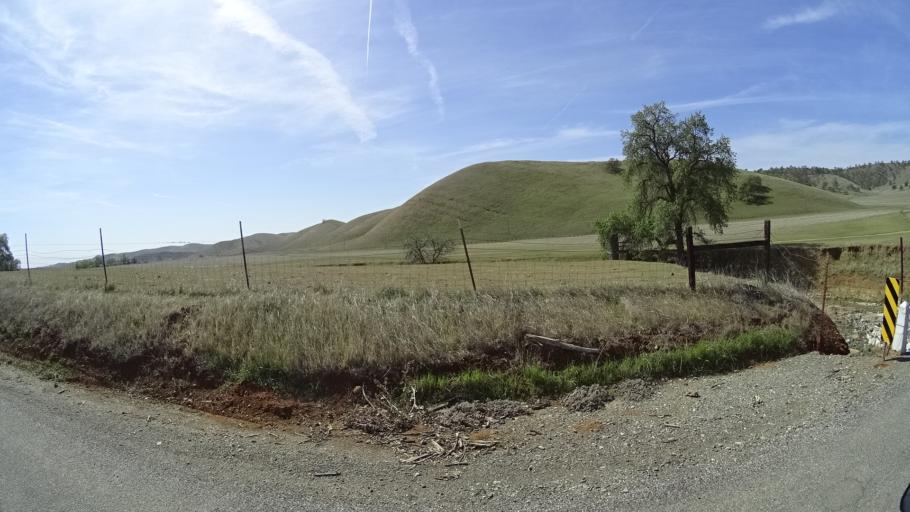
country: US
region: California
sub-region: Glenn County
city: Willows
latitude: 39.5421
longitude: -122.3897
